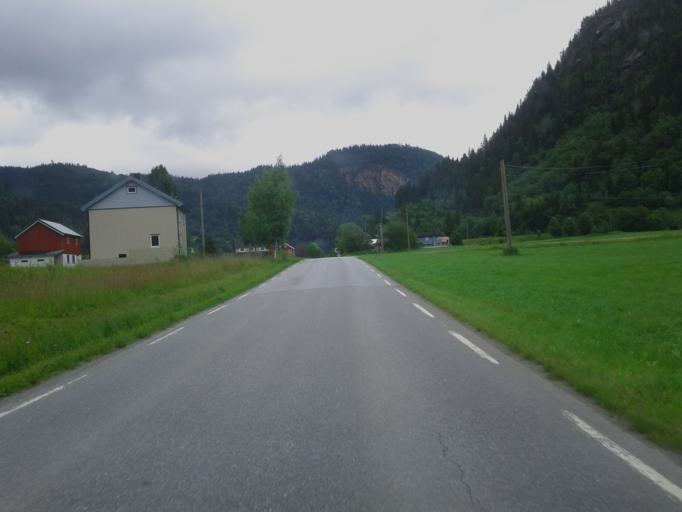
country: NO
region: Sor-Trondelag
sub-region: Midtre Gauldal
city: Storen
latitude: 63.0181
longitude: 10.4155
